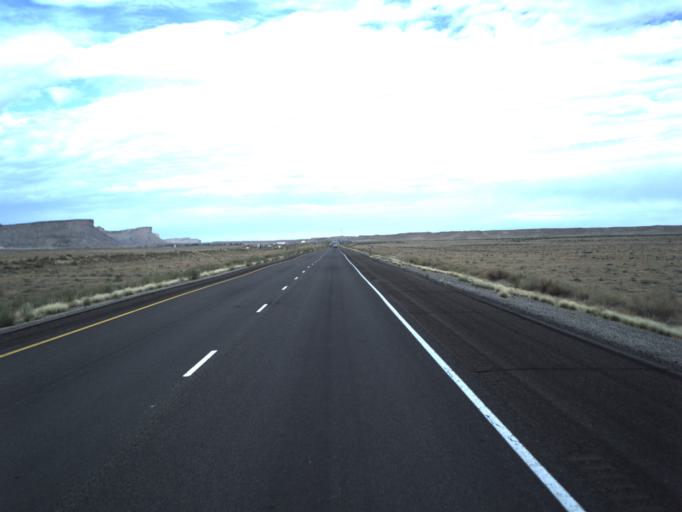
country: US
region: Utah
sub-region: Grand County
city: Moab
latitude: 38.9502
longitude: -109.7744
